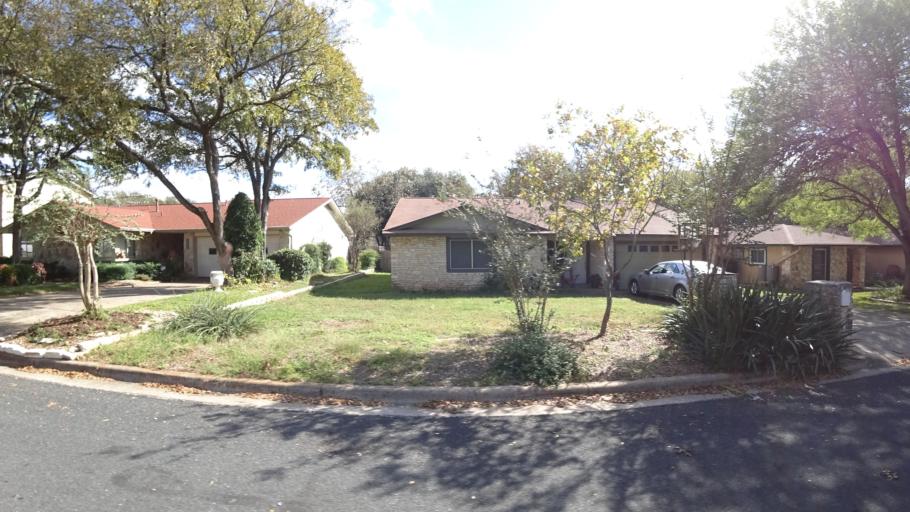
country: US
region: Texas
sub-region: Travis County
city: Wells Branch
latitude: 30.4170
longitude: -97.7251
